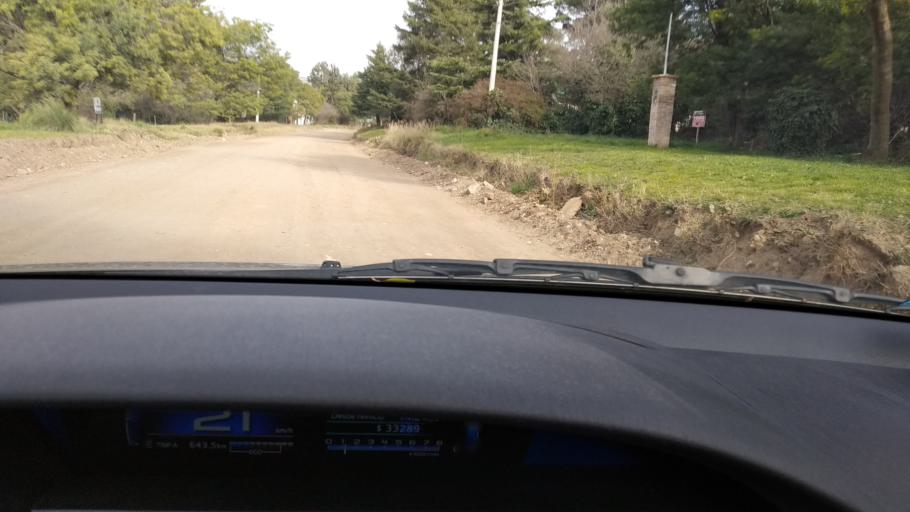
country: AR
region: Buenos Aires
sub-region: Partido de Tornquist
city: Tornquist
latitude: -38.0824
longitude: -61.9282
